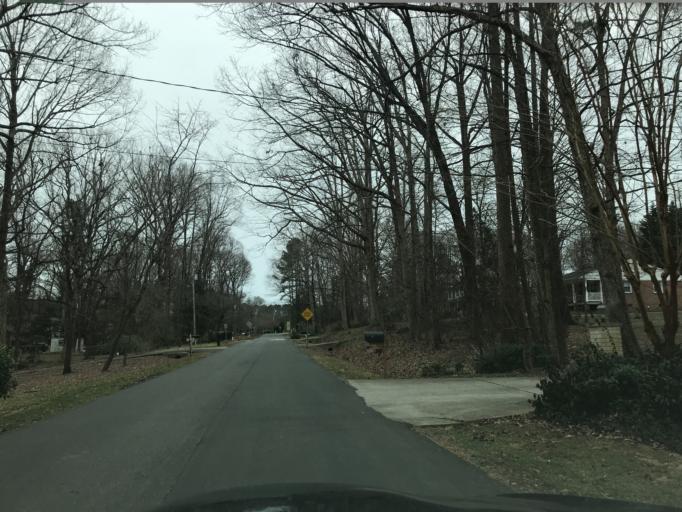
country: US
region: North Carolina
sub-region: Wake County
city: West Raleigh
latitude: 35.8695
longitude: -78.5999
